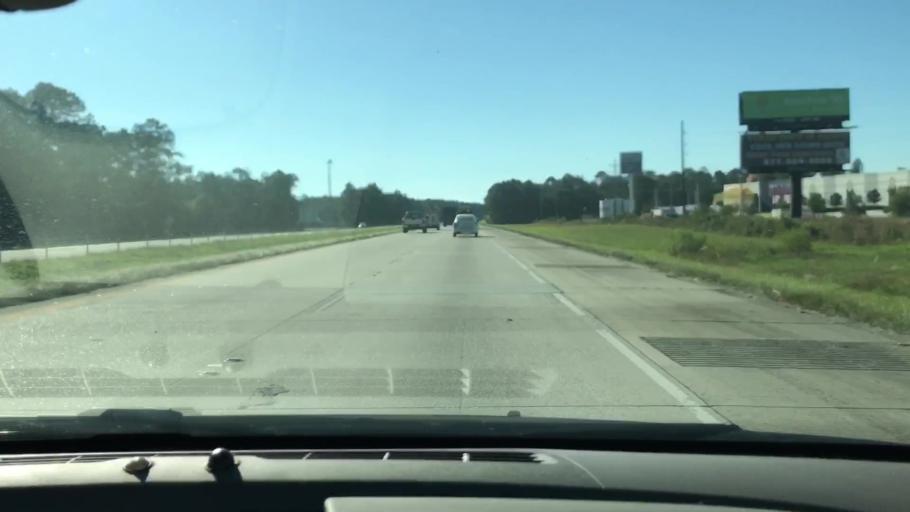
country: US
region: Louisiana
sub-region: Saint Tammany Parish
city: Pearl River
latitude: 30.3470
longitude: -89.7395
